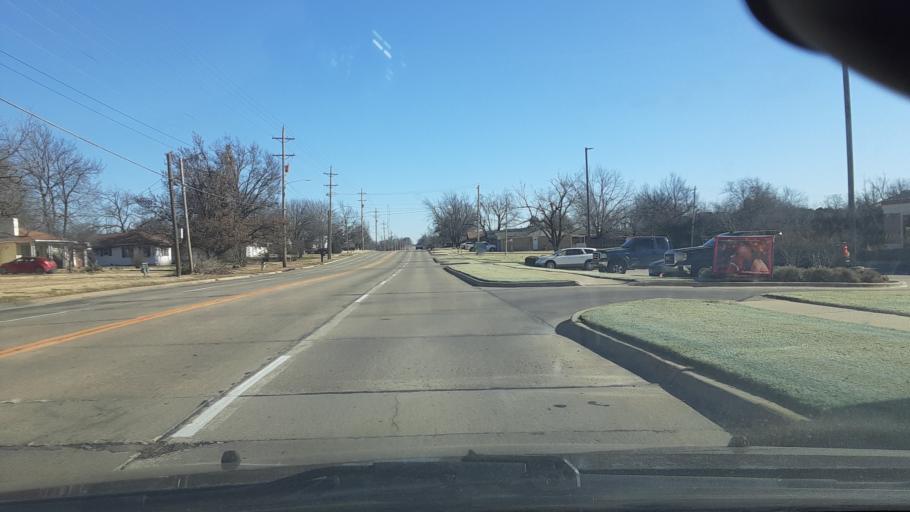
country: US
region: Oklahoma
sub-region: Kay County
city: Ponca City
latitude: 36.7385
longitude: -97.0652
